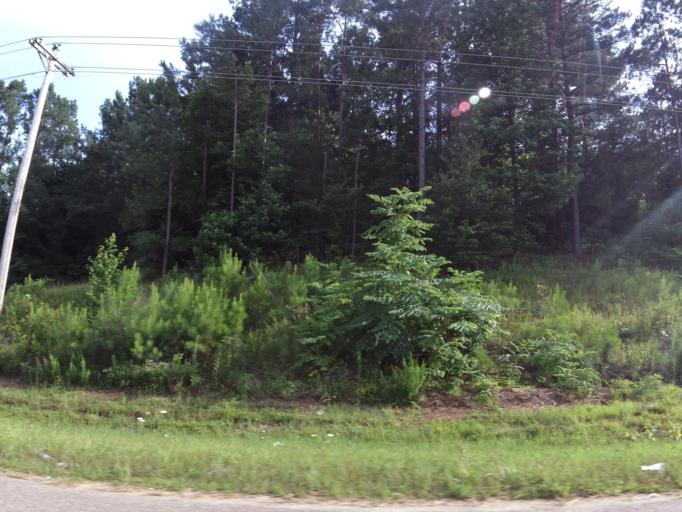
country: US
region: Tennessee
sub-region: Benton County
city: Camden
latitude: 36.0406
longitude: -88.1331
